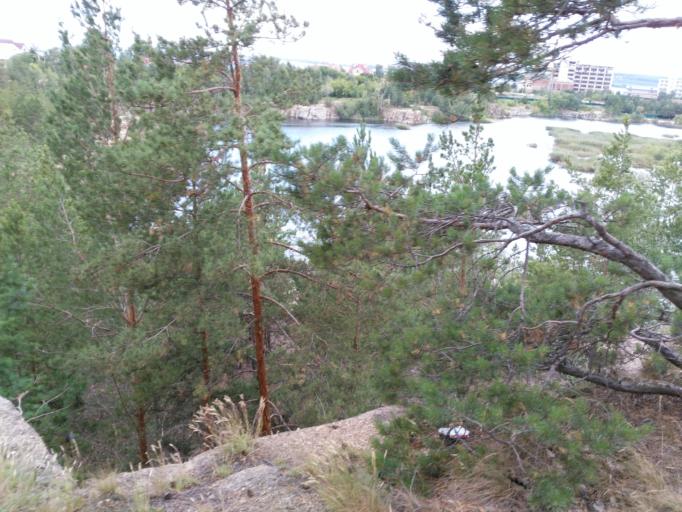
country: RU
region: Chelyabinsk
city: Novosineglazovskiy
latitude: 55.1227
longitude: 61.3388
